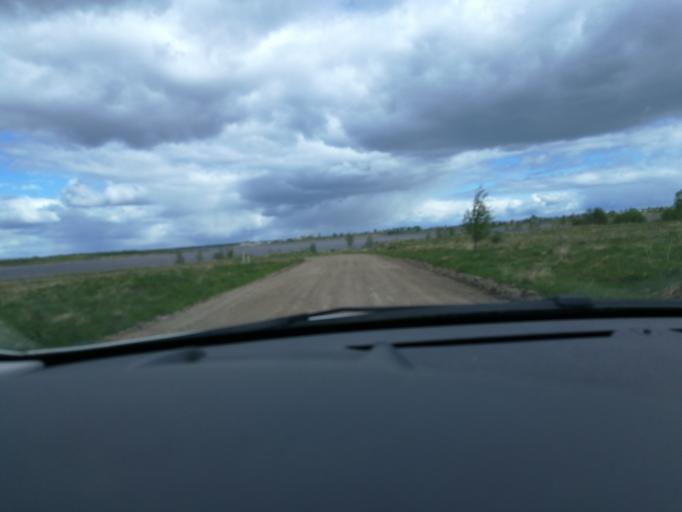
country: RU
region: Arkhangelskaya
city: Lukovetskiy
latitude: 64.2583
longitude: 41.8022
